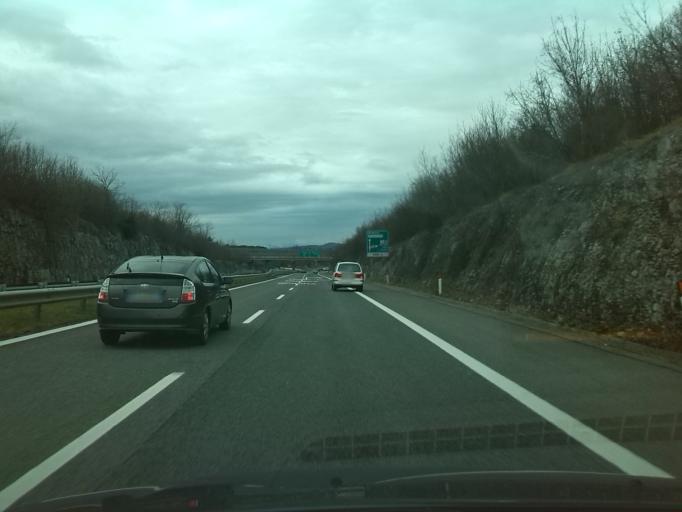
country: IT
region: Friuli Venezia Giulia
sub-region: Provincia di Trieste
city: Villa Opicina
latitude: 45.6701
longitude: 13.8229
